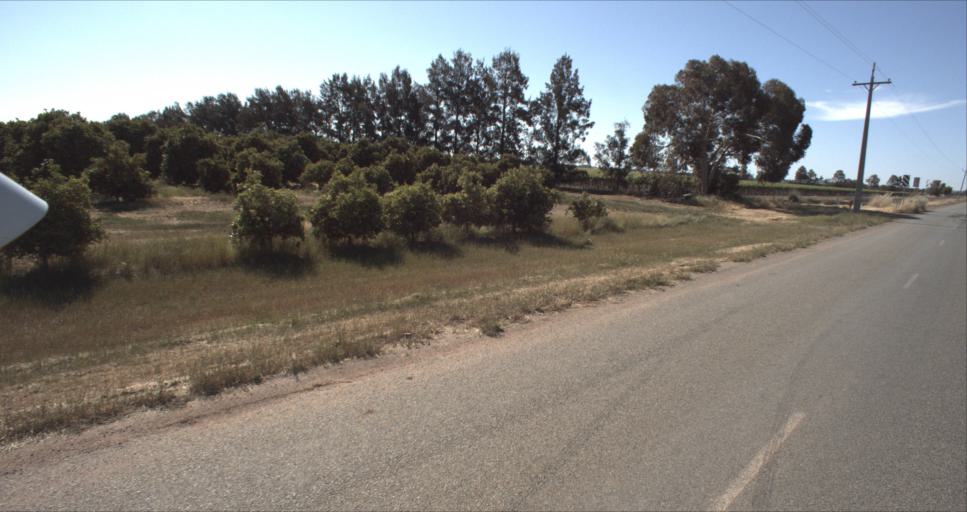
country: AU
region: New South Wales
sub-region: Leeton
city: Leeton
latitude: -34.5851
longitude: 146.3791
